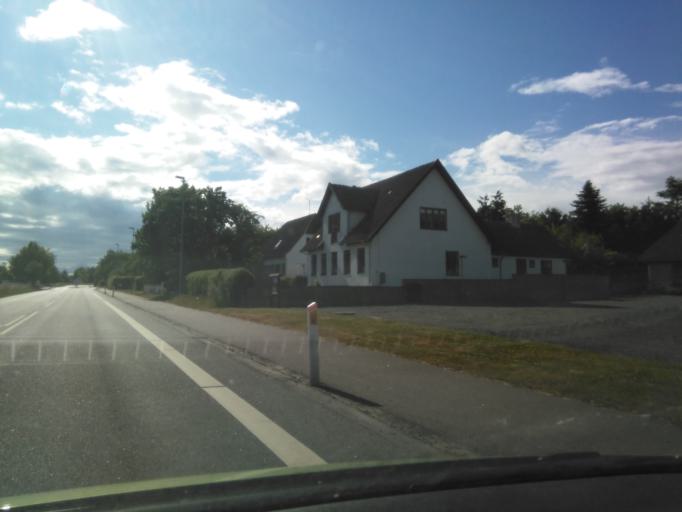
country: DK
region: Capital Region
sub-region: Bornholm Kommune
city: Akirkeby
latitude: 55.1384
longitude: 15.0232
